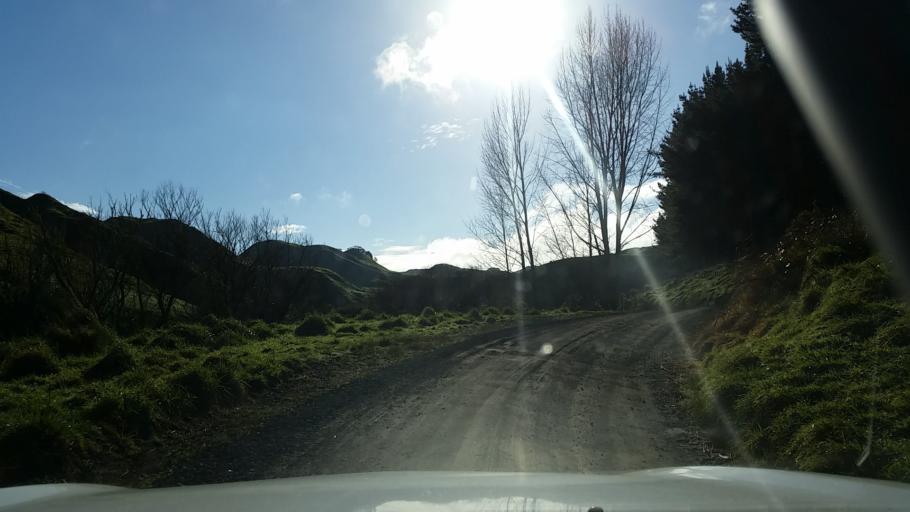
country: NZ
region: Taranaki
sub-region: South Taranaki District
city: Eltham
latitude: -39.5040
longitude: 174.4033
